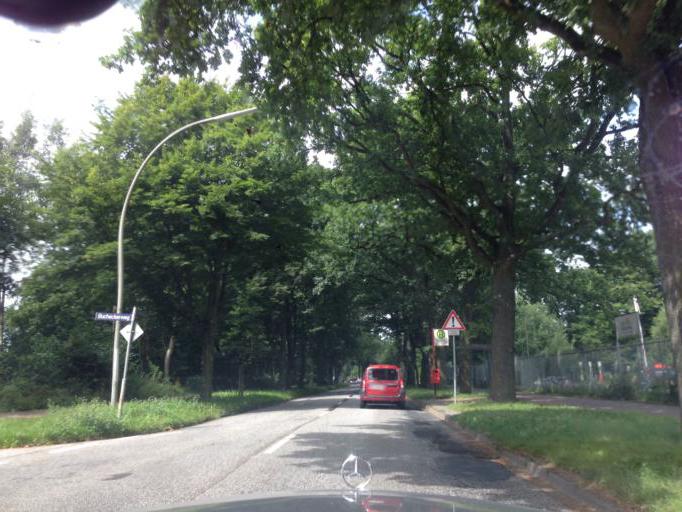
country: DE
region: Hamburg
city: Sasel
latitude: 53.6292
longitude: 10.1078
